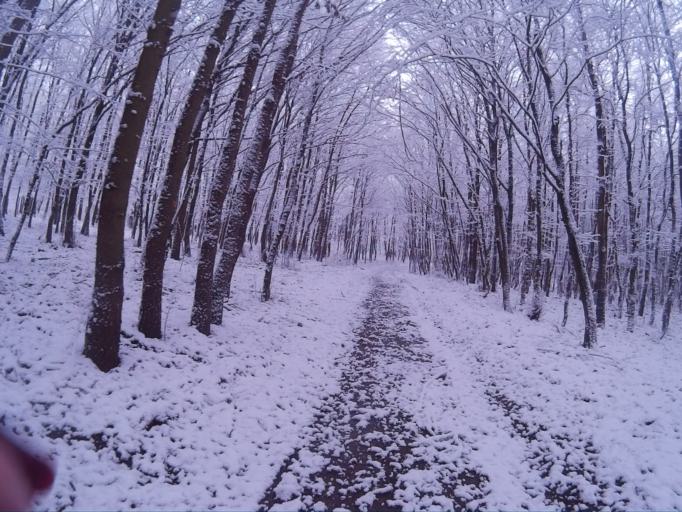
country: HU
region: Komarom-Esztergom
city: Tarjan
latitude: 47.5813
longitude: 18.4641
